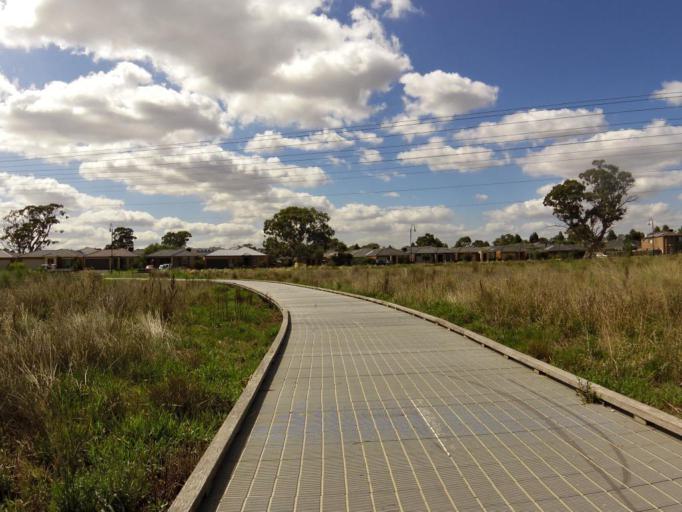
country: AU
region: Victoria
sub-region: Whittlesea
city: Mernda
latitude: -37.6341
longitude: 145.0885
